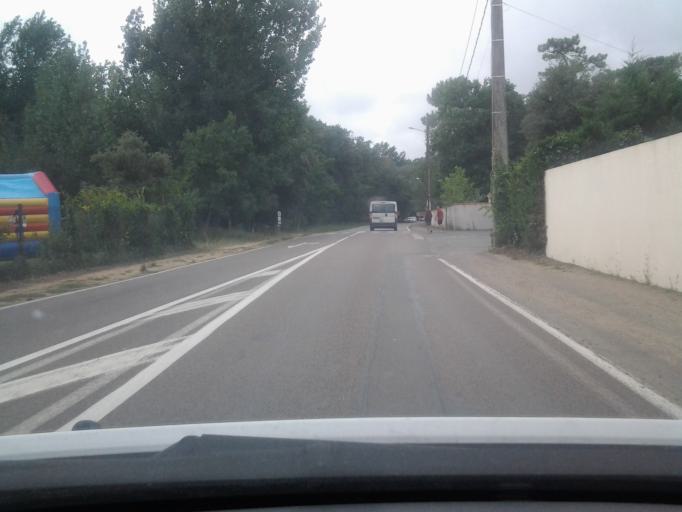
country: FR
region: Pays de la Loire
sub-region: Departement de la Vendee
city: Longeville-sur-Mer
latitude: 46.4043
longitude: -1.4887
